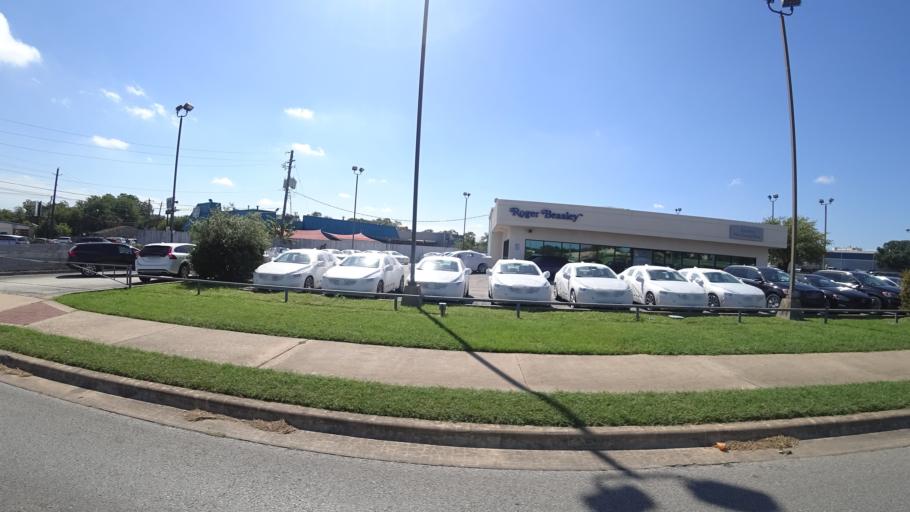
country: US
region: Texas
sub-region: Travis County
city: Austin
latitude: 30.3210
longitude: -97.6972
